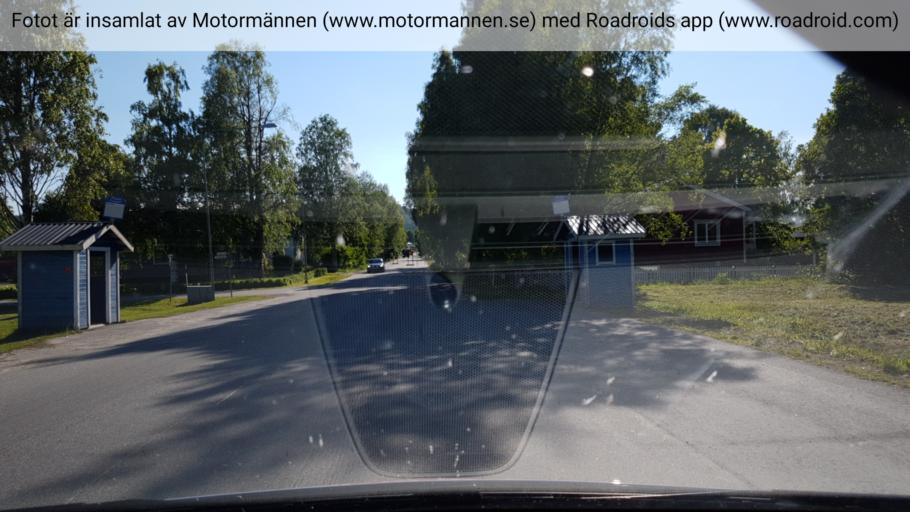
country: SE
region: Vaesterbotten
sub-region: Vannas Kommun
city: Vannasby
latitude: 63.9130
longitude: 19.8296
